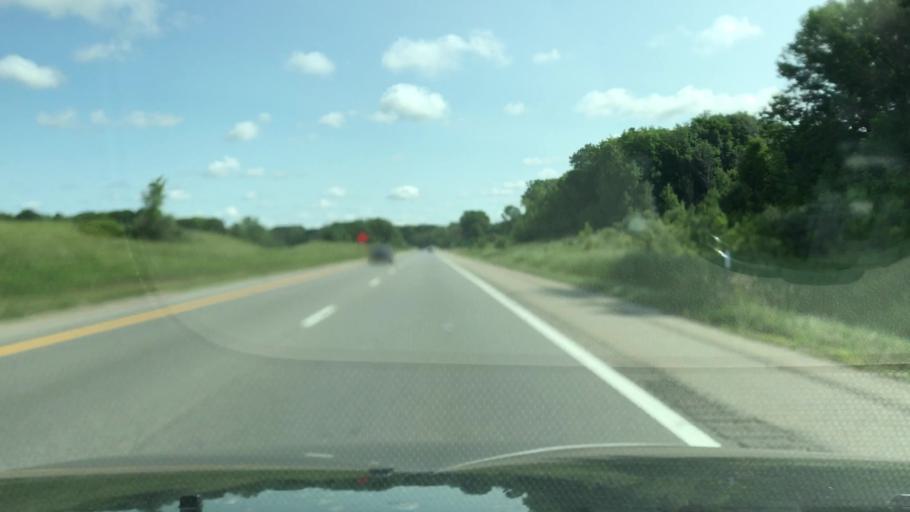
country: US
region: Michigan
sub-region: Kent County
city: Cedar Springs
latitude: 43.2306
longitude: -85.5691
